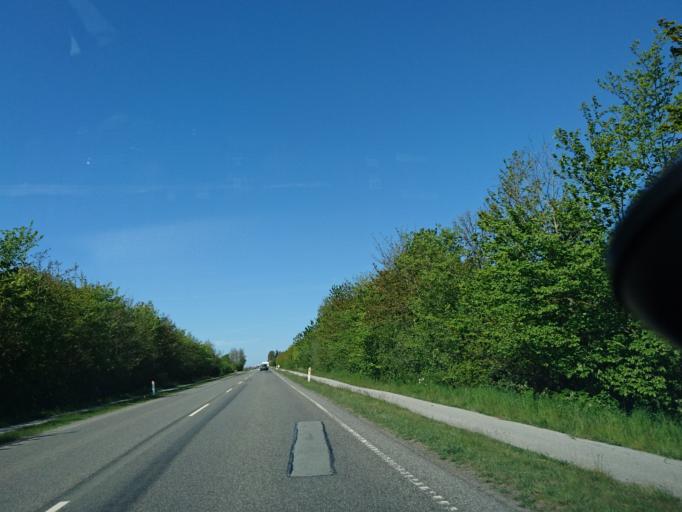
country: DK
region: North Denmark
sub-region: Hjorring Kommune
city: Tars
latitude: 57.4564
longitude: 10.0736
